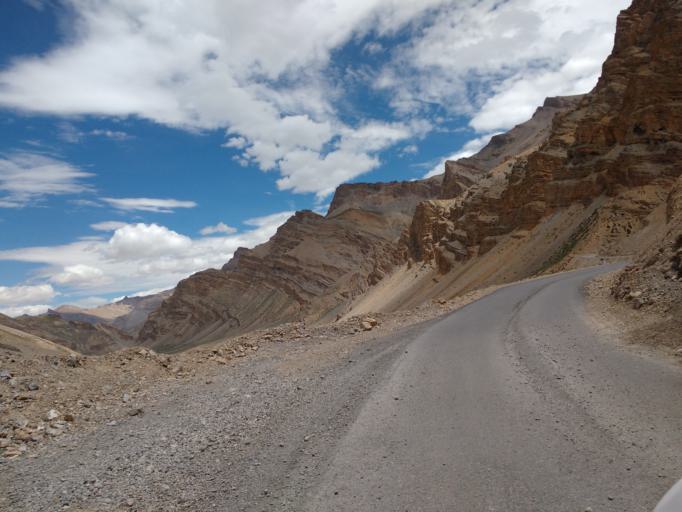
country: IN
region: Himachal Pradesh
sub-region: Lahul and Spiti
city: Kyelang
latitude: 33.0392
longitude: 77.5910
